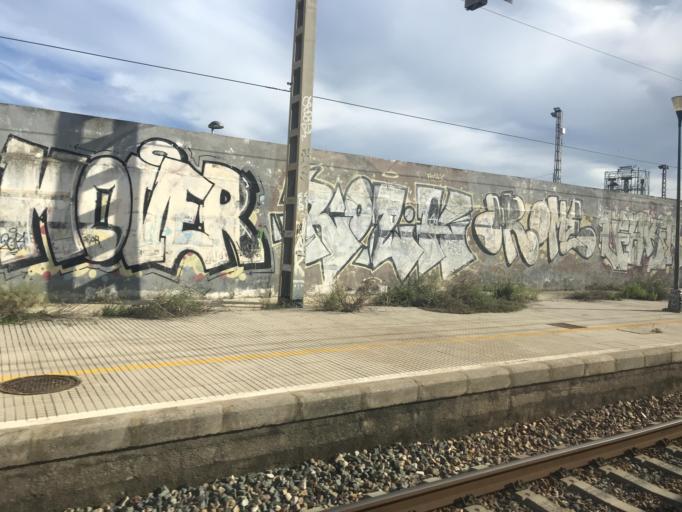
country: ES
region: Valencia
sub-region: Provincia de Castello
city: Benicarlo
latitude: 40.4289
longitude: 0.4161
